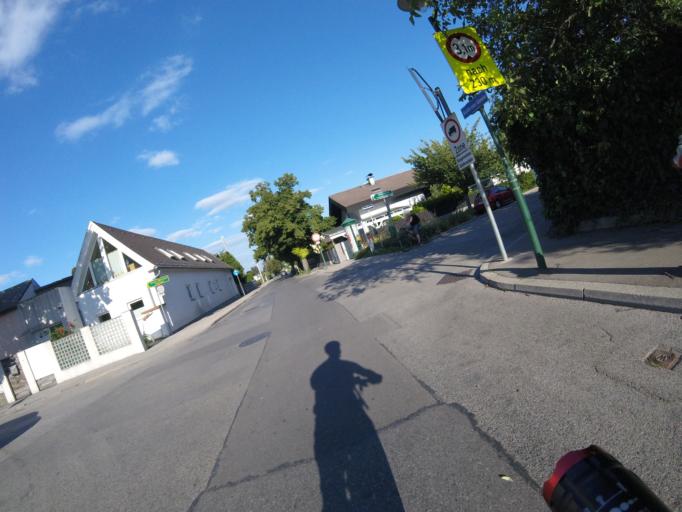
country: AT
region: Lower Austria
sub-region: Politischer Bezirk Modling
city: Modling
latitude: 48.0763
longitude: 16.2985
